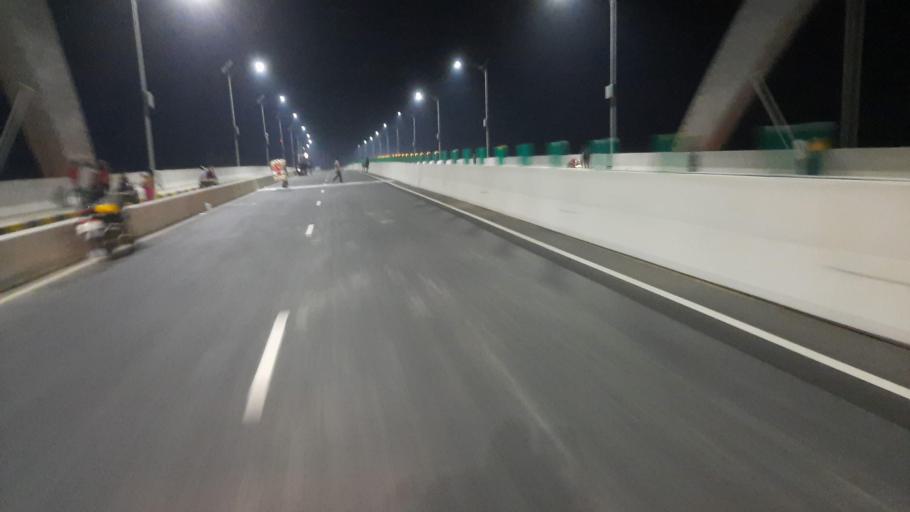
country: BD
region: Khulna
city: Kalia
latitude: 23.1927
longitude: 89.6902
